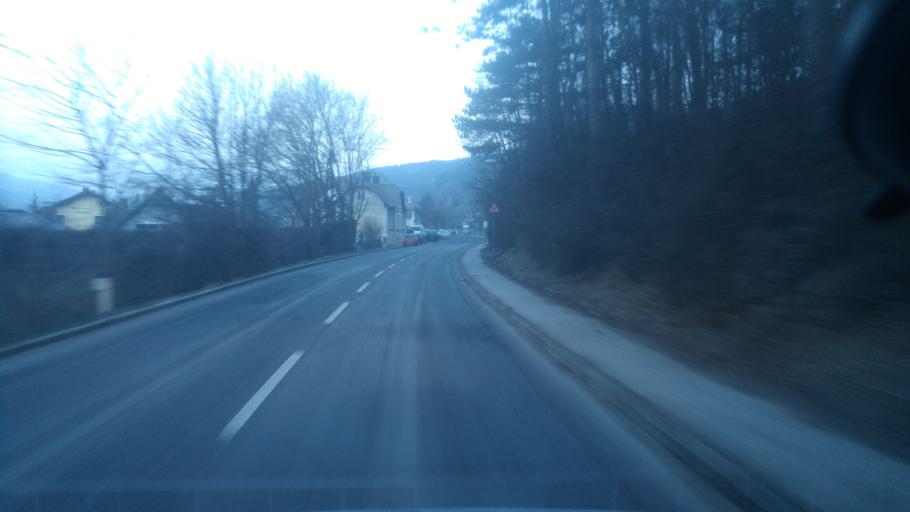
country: AT
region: Lower Austria
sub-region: Politischer Bezirk Baden
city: Pottenstein
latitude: 47.9542
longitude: 16.1038
